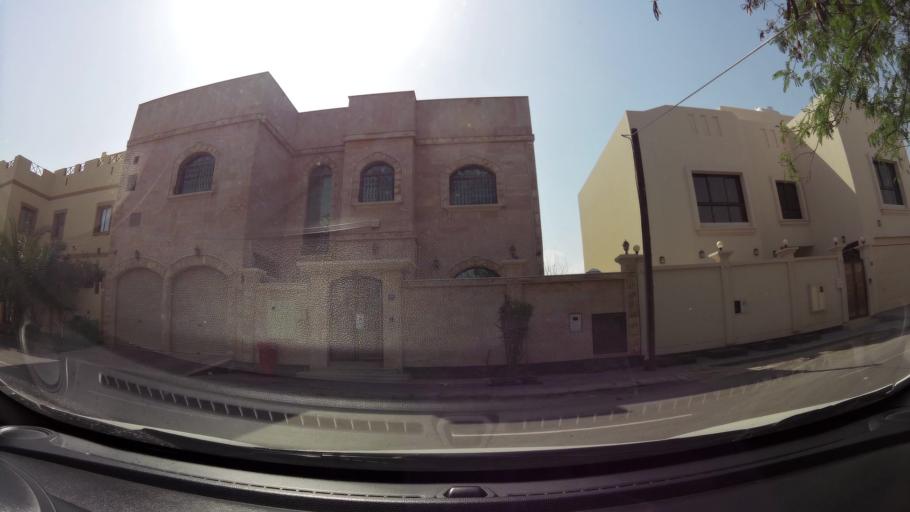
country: BH
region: Manama
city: Jidd Hafs
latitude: 26.2083
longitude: 50.4627
